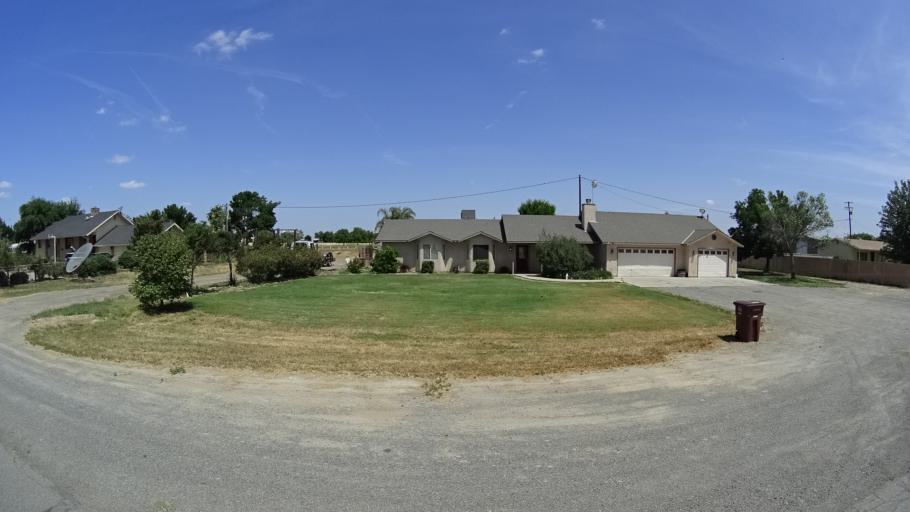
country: US
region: California
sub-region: Tulare County
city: Goshen
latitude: 36.2978
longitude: -119.4889
